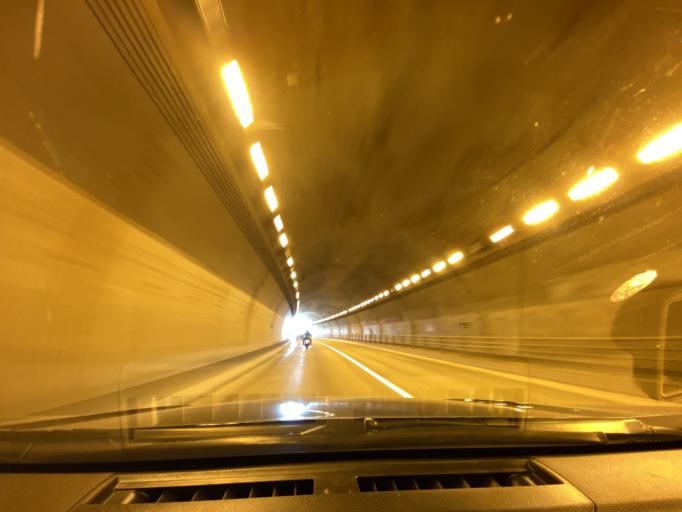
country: JP
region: Hokkaido
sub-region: Asahikawa-shi
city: Asahikawa
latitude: 43.8470
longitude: 142.4560
